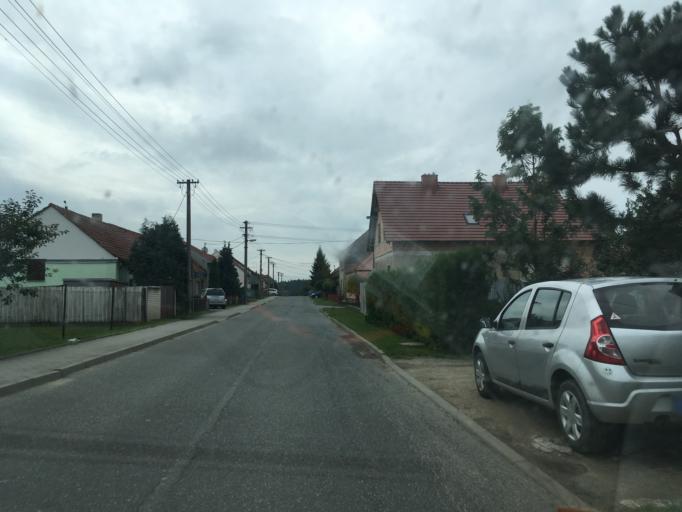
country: CZ
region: South Moravian
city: Zbraslav
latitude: 49.1898
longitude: 16.2557
